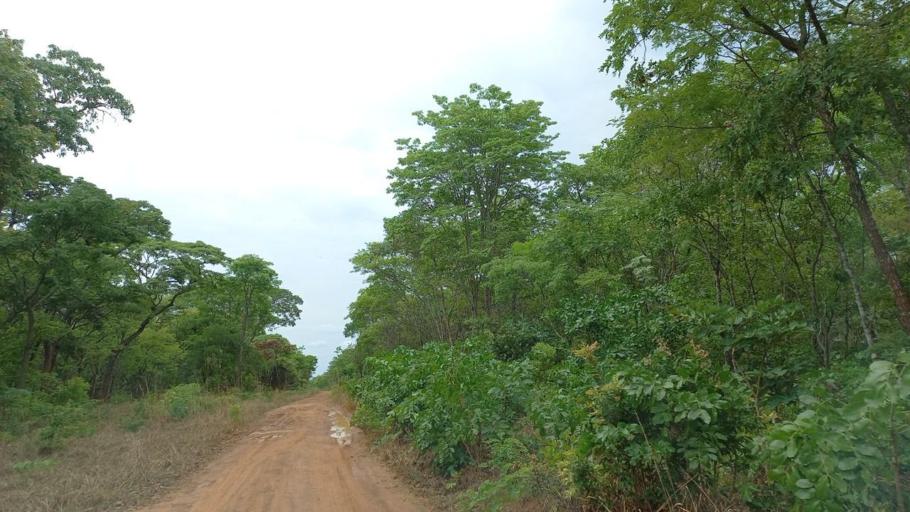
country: ZM
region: North-Western
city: Kalengwa
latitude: -13.5741
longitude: 24.9707
